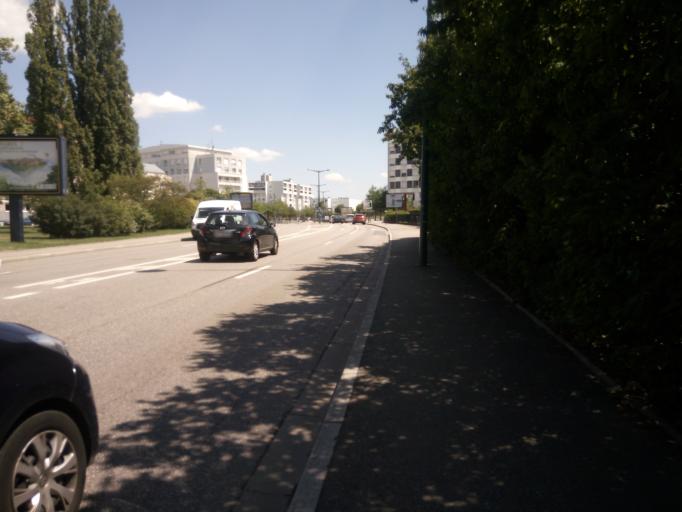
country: FR
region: Lorraine
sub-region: Departement de Meurthe-et-Moselle
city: Villers-les-Nancy
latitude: 48.6679
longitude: 6.1624
